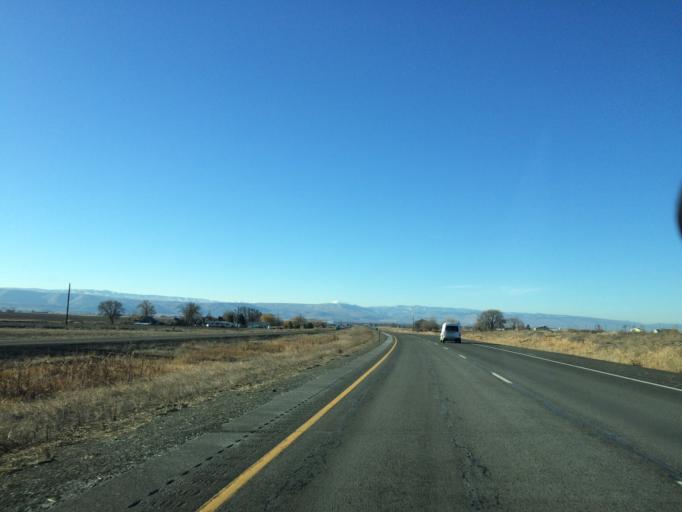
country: US
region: Washington
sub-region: Kittitas County
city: Kittitas
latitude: 46.9730
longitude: -120.3744
